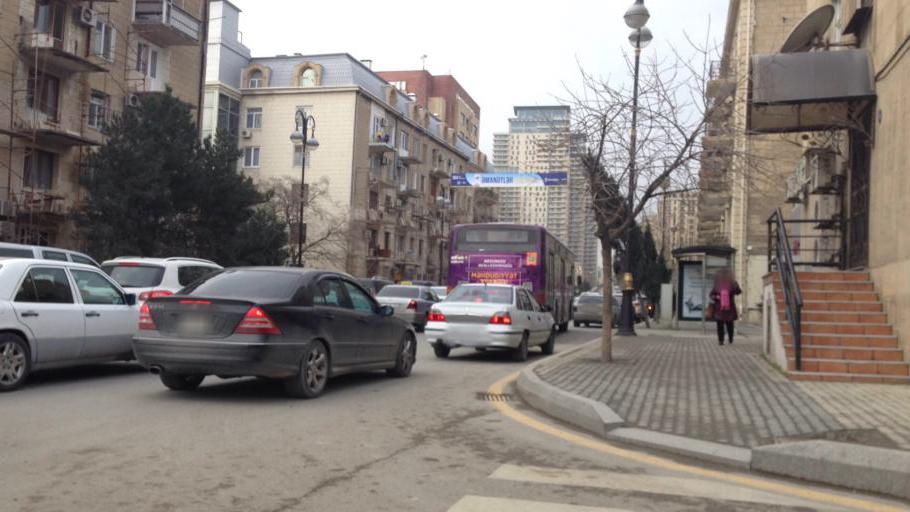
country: AZ
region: Baki
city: Baku
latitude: 40.3780
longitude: 49.8669
